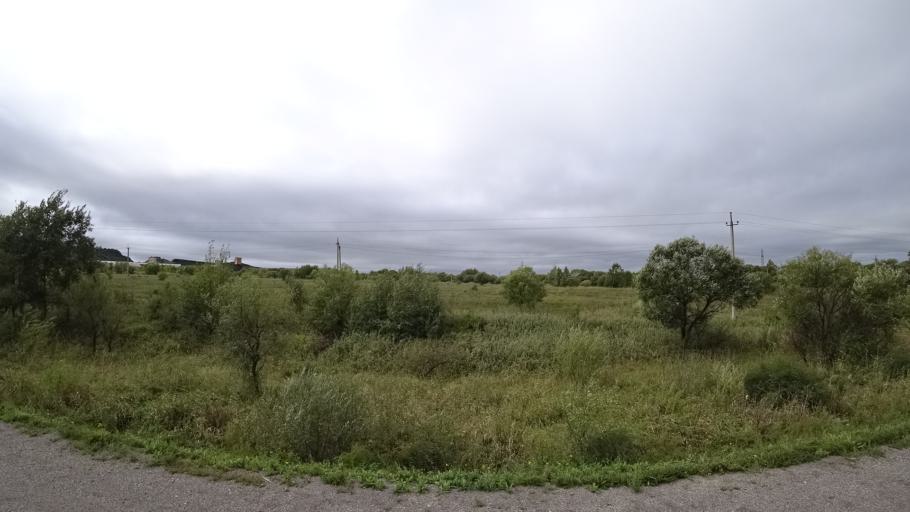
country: RU
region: Primorskiy
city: Monastyrishche
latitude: 44.1740
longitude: 132.4413
